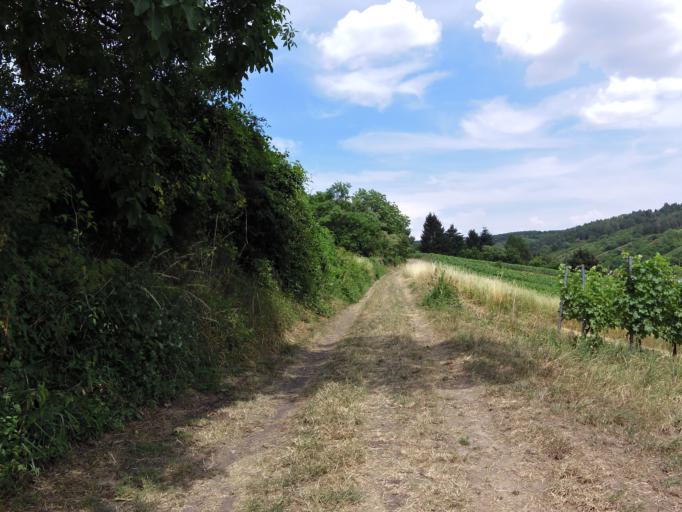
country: DE
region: Bavaria
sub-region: Regierungsbezirk Unterfranken
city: Gerbrunn
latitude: 49.7672
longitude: 9.9891
